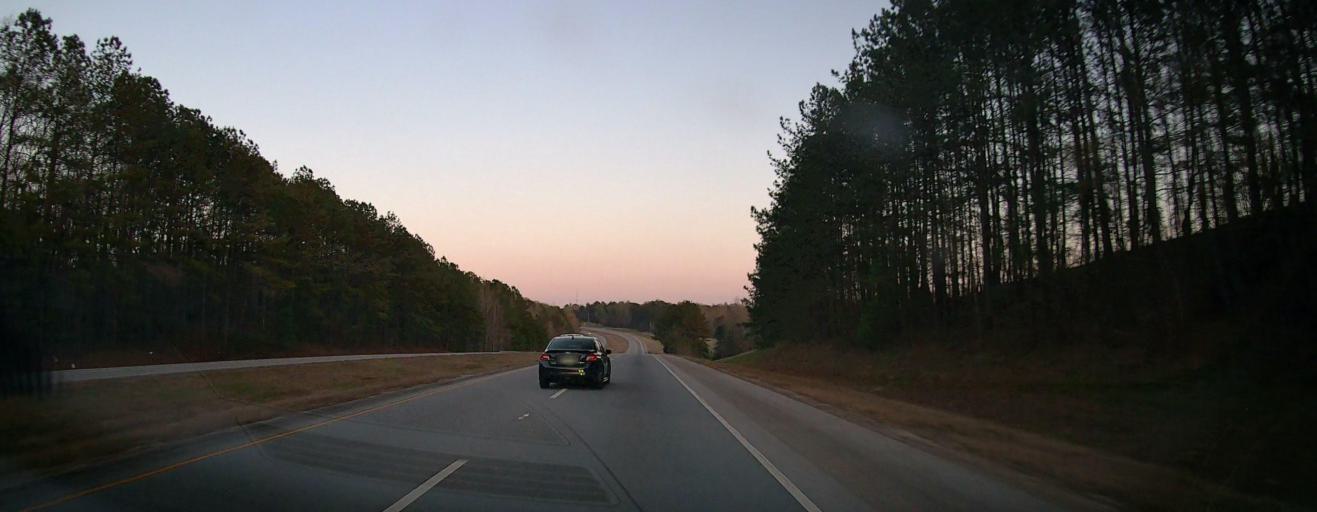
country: US
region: Alabama
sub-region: Tallapoosa County
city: Alexander City
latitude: 32.9093
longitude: -85.9393
